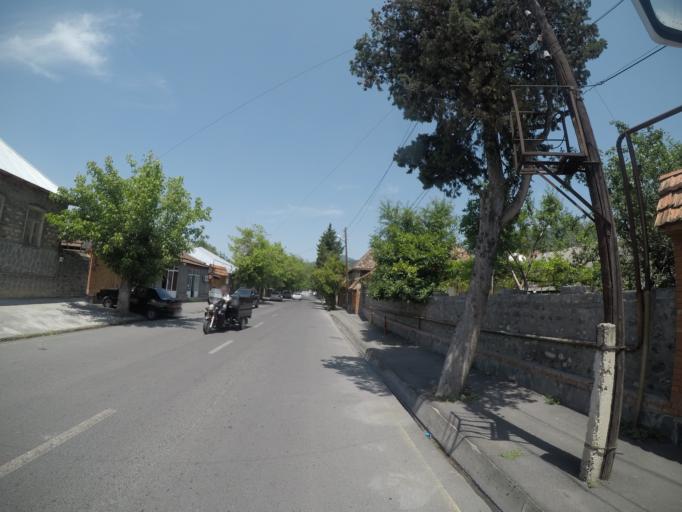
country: AZ
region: Qakh Rayon
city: Qax
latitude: 41.4171
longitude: 46.9195
